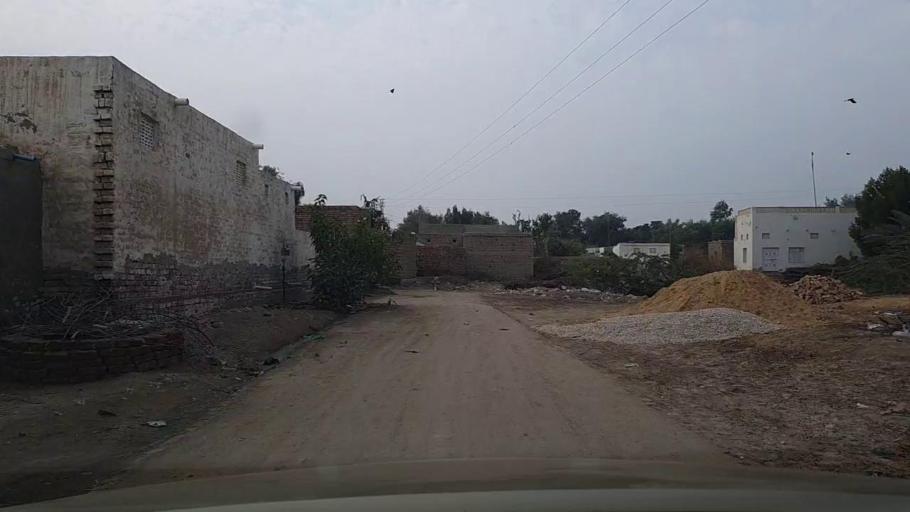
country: PK
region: Sindh
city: Sanghar
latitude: 26.1701
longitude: 68.9564
